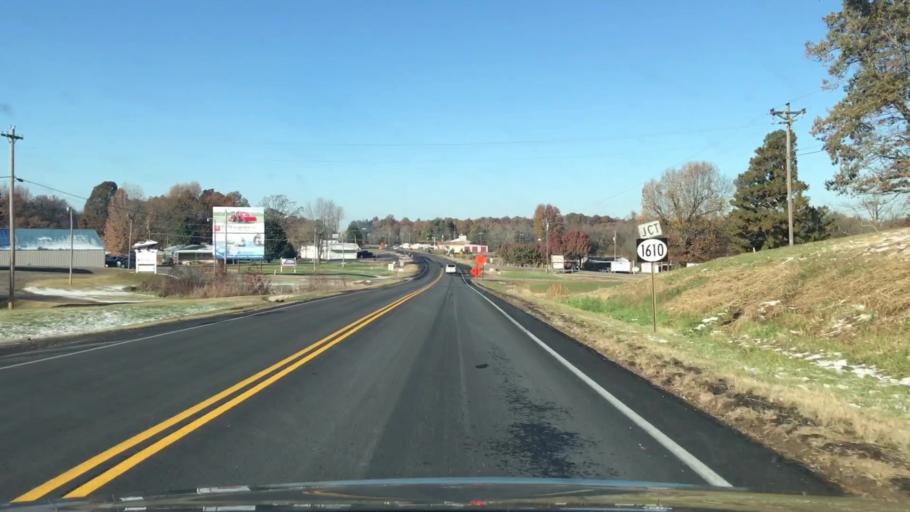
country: US
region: Kentucky
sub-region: Livingston County
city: Ledbetter
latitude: 37.0062
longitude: -88.4273
